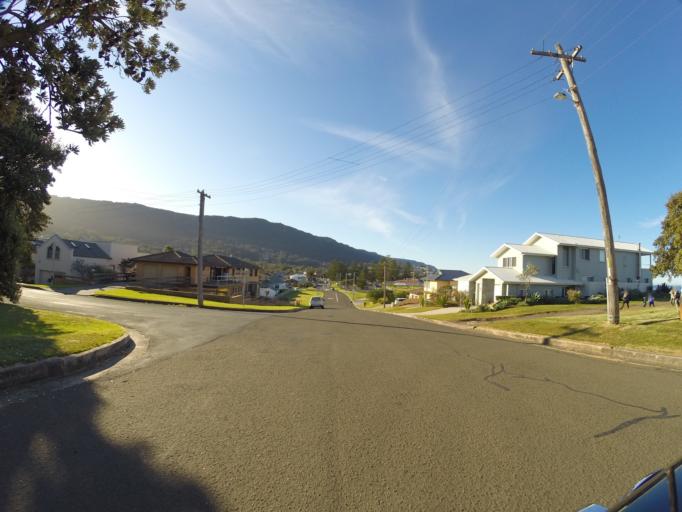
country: AU
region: New South Wales
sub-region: Wollongong
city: Bulli
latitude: -34.3196
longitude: 150.9257
